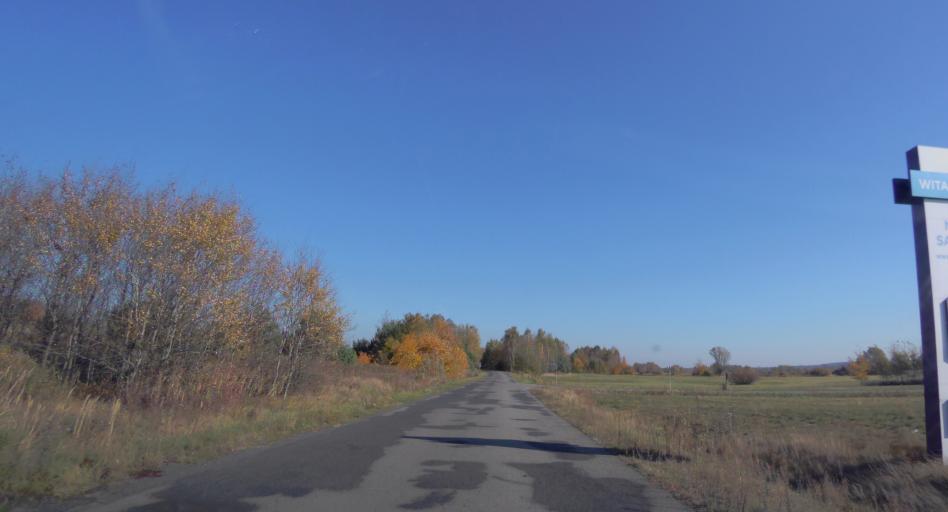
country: PL
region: Subcarpathian Voivodeship
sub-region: Powiat lezajski
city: Wola Zarczycka
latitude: 50.2702
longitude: 22.2543
